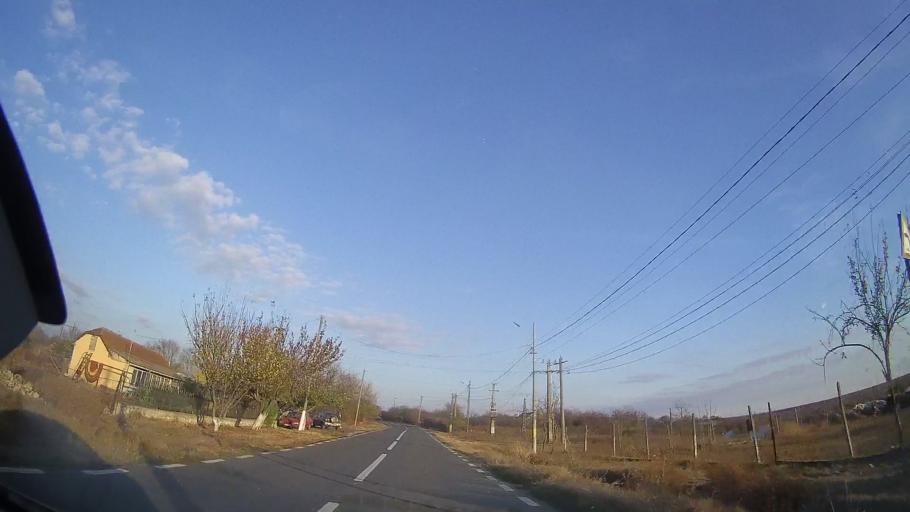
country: RO
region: Constanta
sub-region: Comuna Chirnogeni
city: Plopeni
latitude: 43.9507
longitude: 28.1845
